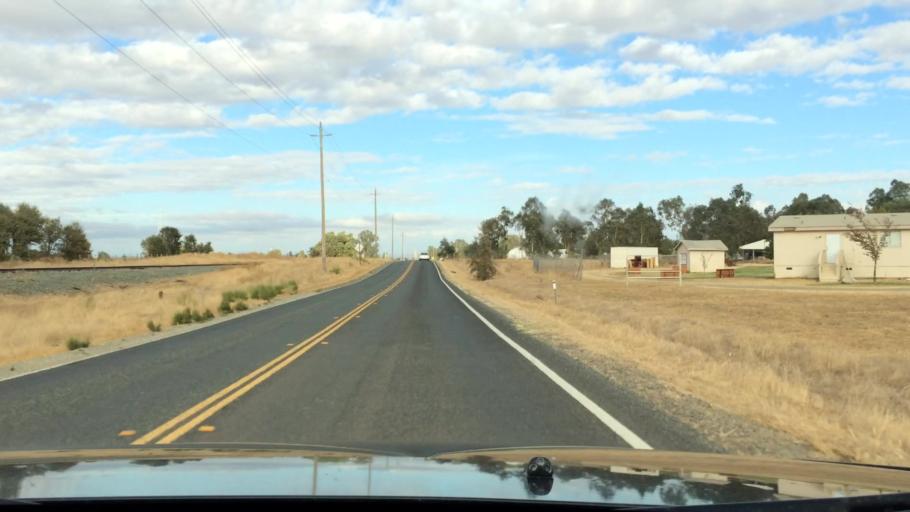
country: US
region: California
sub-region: Sacramento County
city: Herald
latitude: 38.3033
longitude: -121.2307
